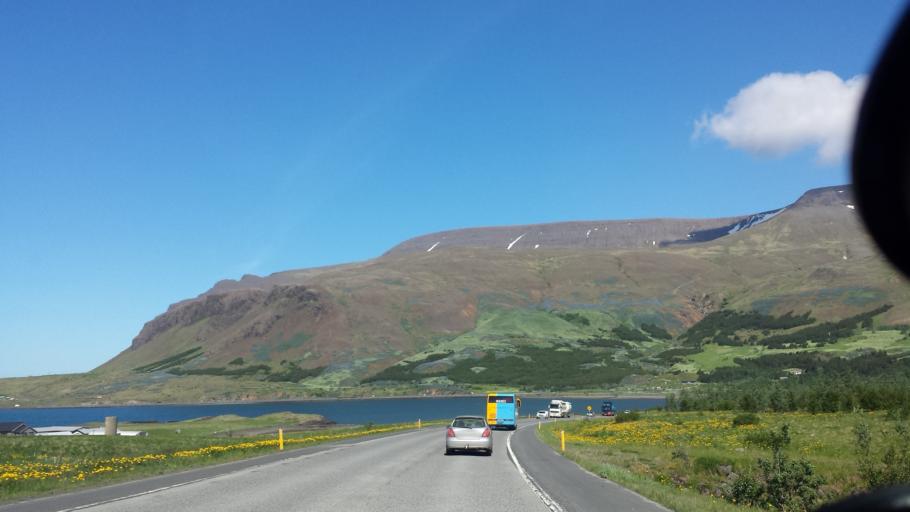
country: IS
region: Capital Region
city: Mosfellsbaer
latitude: 64.1986
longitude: -21.7068
